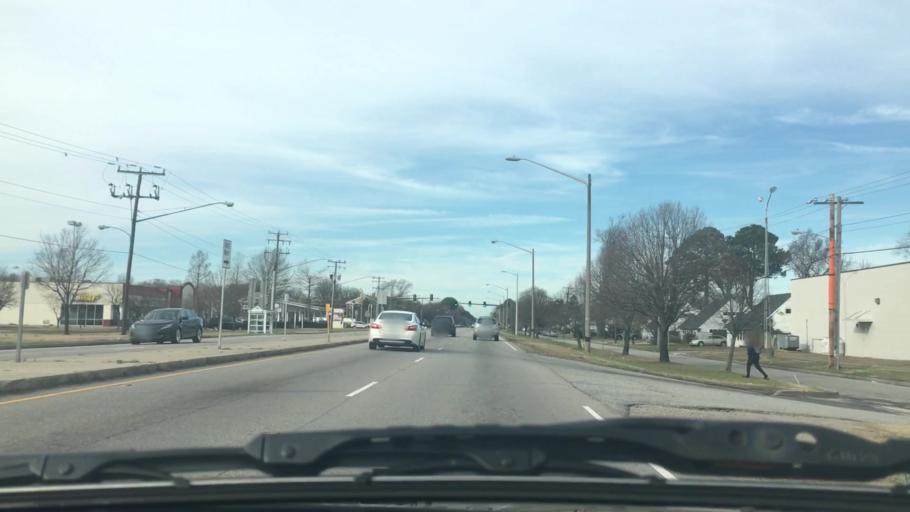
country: US
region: Virginia
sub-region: City of Norfolk
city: Norfolk
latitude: 36.8956
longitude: -76.2241
